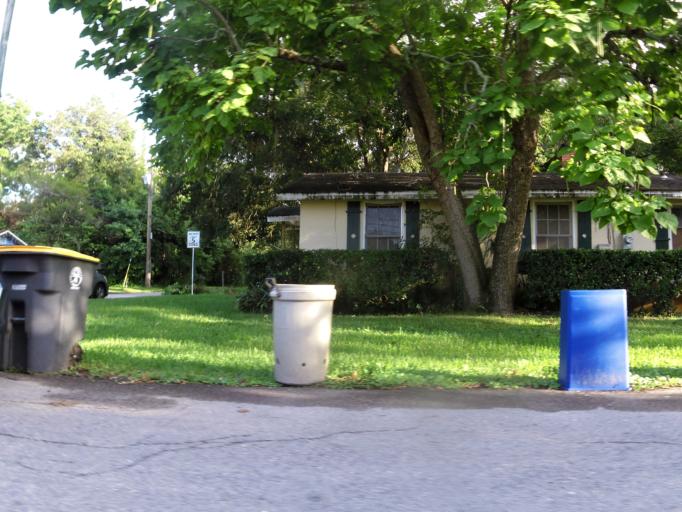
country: US
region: Florida
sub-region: Duval County
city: Jacksonville
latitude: 30.3009
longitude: -81.6264
